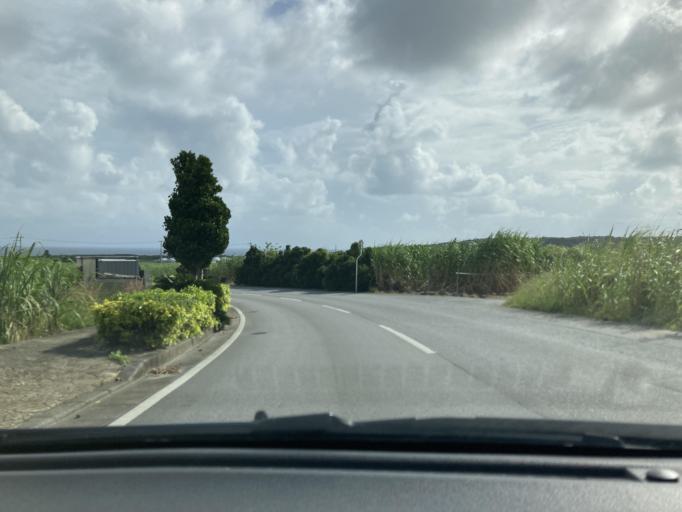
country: JP
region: Okinawa
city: Itoman
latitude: 26.0940
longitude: 127.6932
